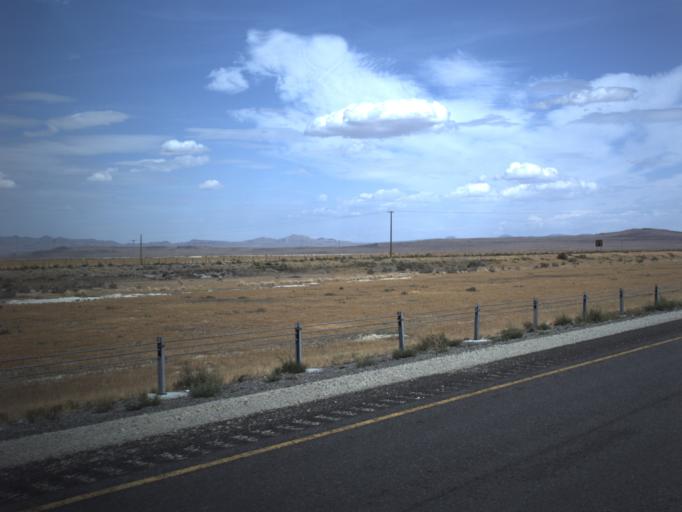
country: US
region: Utah
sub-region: Tooele County
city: Grantsville
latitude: 40.7262
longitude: -113.2370
